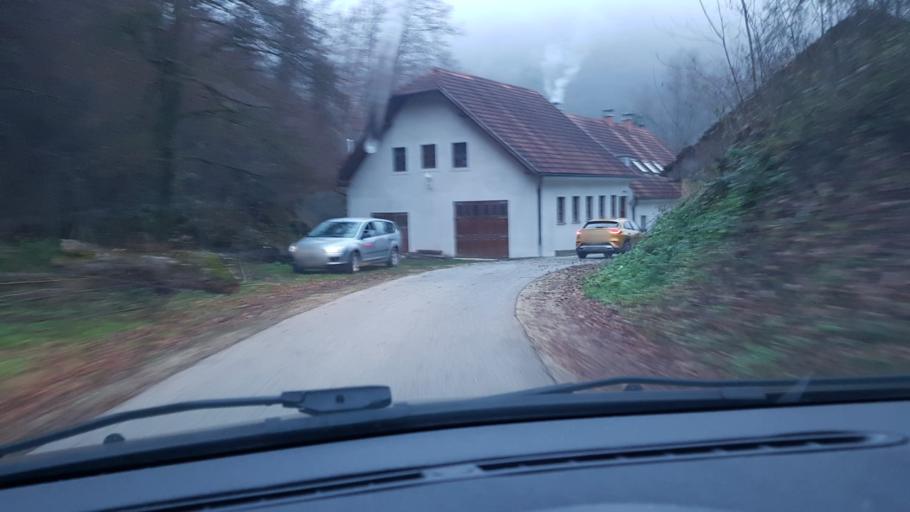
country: HR
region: Krapinsko-Zagorska
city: Pregrada
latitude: 46.1904
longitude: 15.7395
